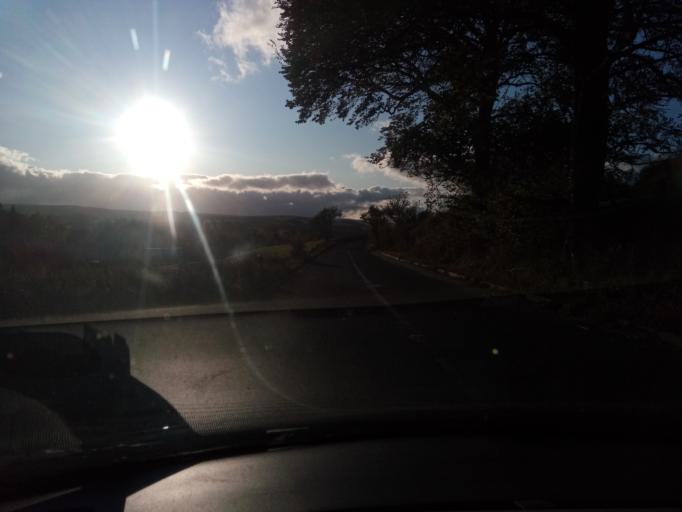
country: GB
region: England
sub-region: County Durham
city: Stanhope
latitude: 54.7462
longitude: -2.0345
